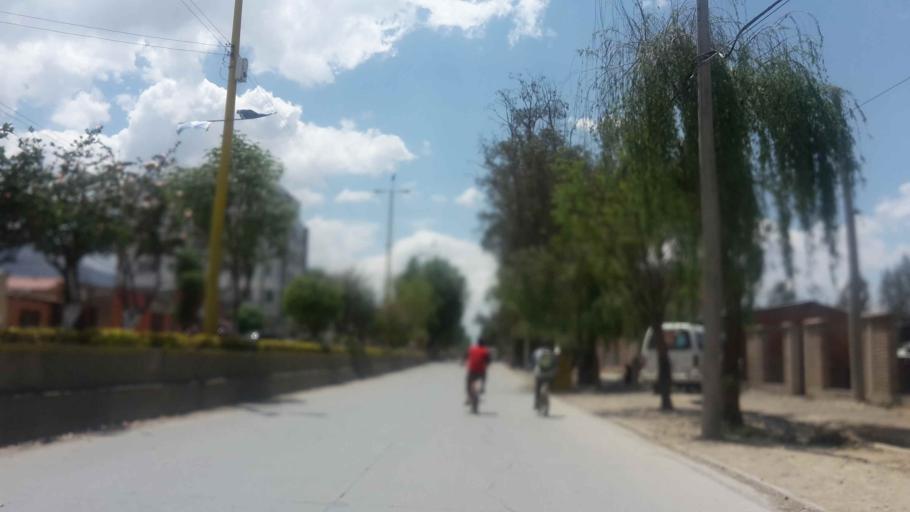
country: BO
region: Cochabamba
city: Cochabamba
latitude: -17.3466
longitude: -66.2015
